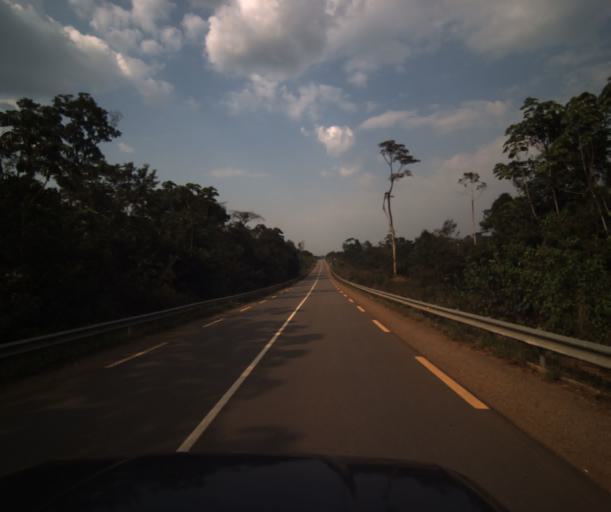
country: CM
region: Centre
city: Akono
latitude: 3.6341
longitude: 11.3253
